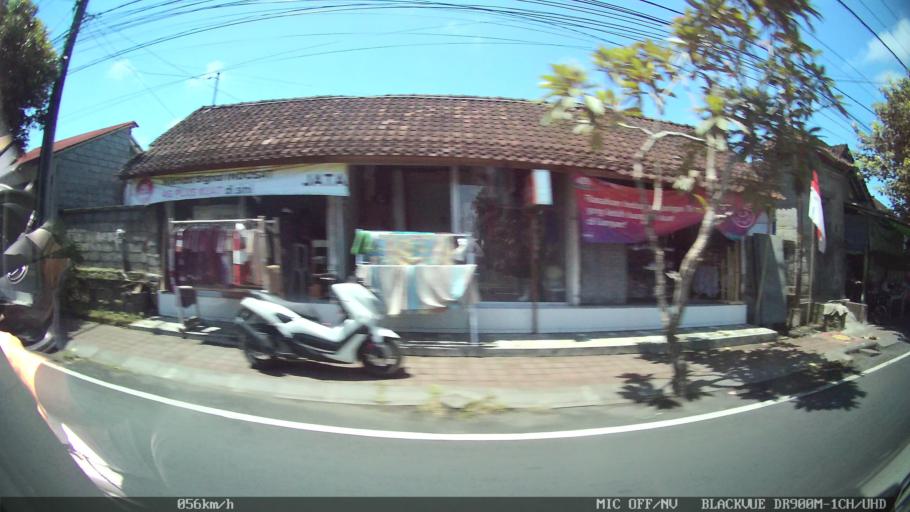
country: ID
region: Bali
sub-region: Kabupaten Gianyar
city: Ubud
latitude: -8.5614
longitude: 115.3089
